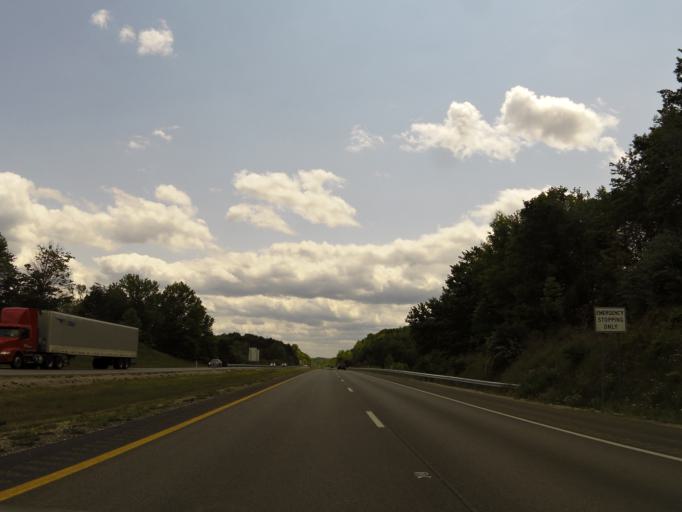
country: US
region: West Virginia
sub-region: Kanawha County
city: Sissonville
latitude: 38.6532
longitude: -81.6526
